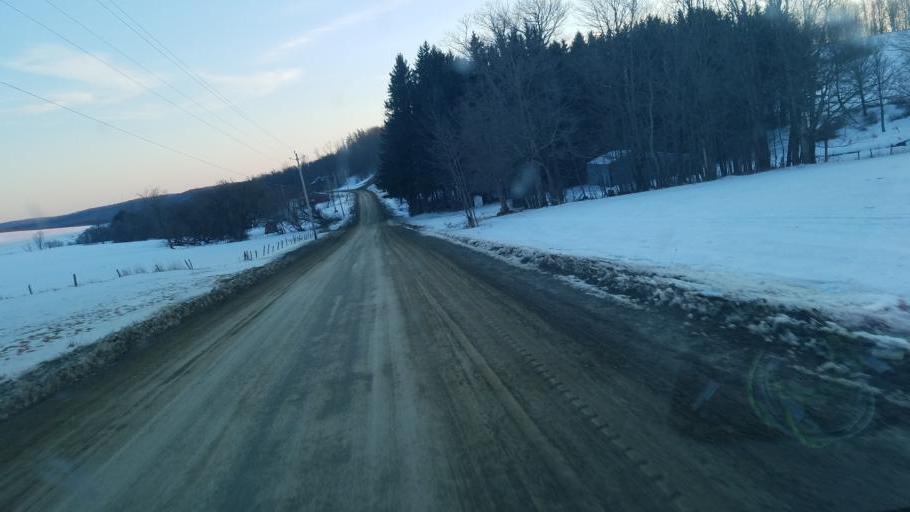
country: US
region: Pennsylvania
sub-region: Tioga County
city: Westfield
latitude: 42.0179
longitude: -77.6568
